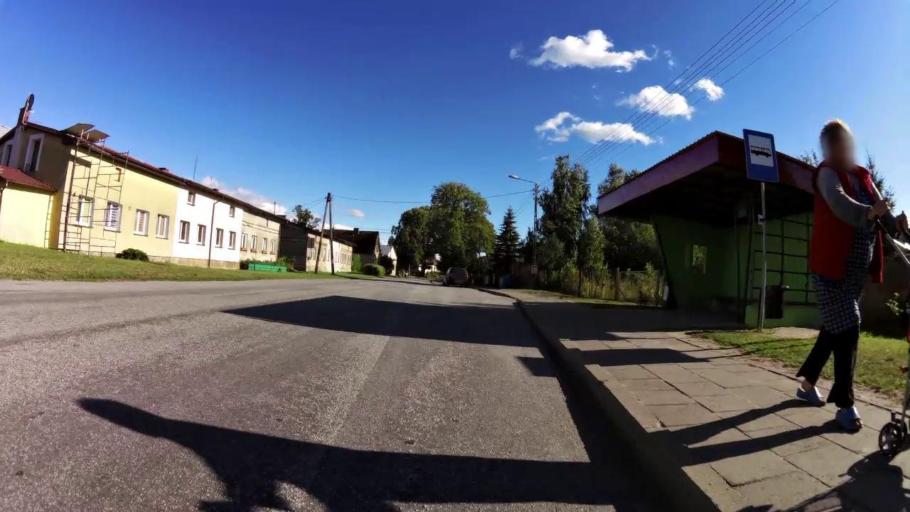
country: PL
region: West Pomeranian Voivodeship
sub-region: Powiat swidwinski
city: Swidwin
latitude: 53.7599
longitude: 15.6942
